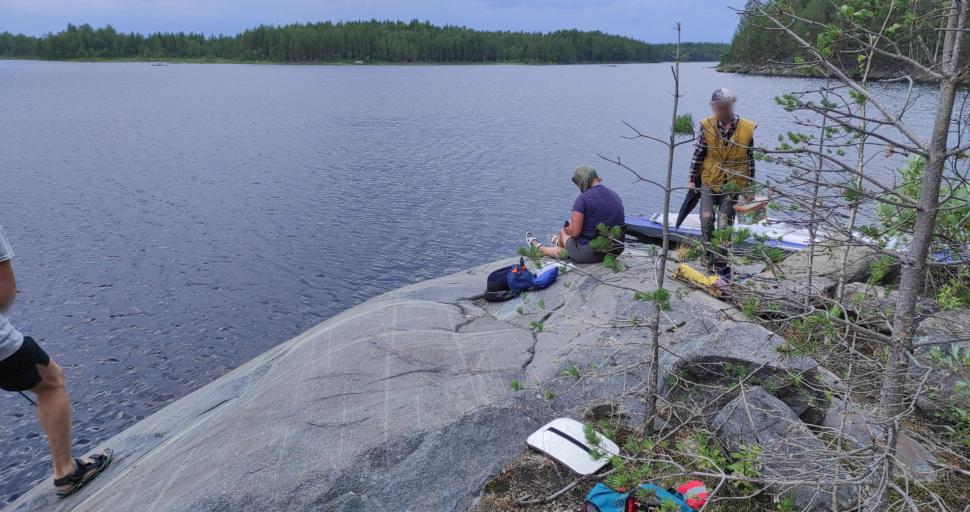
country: RU
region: Murmansk
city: Poyakonda
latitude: 66.6855
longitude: 32.7274
